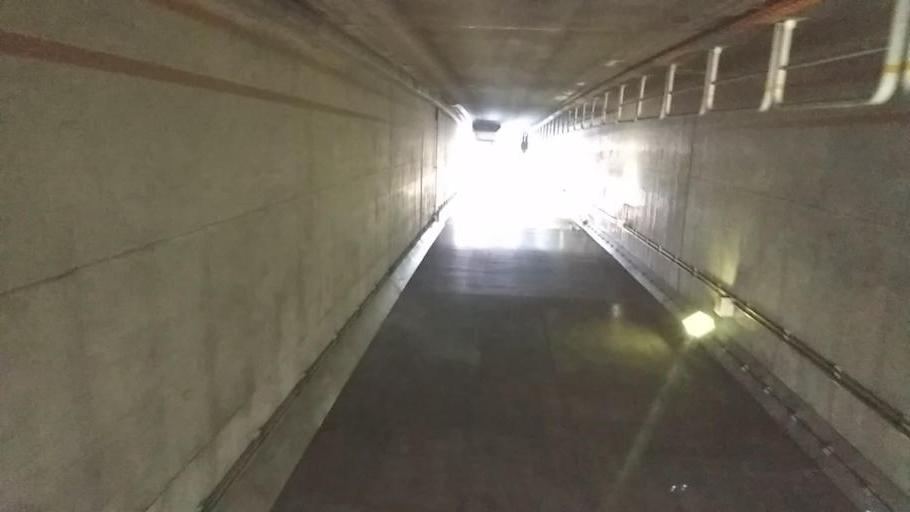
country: JP
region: Tokyo
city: Hachioji
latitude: 35.6252
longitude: 139.2638
